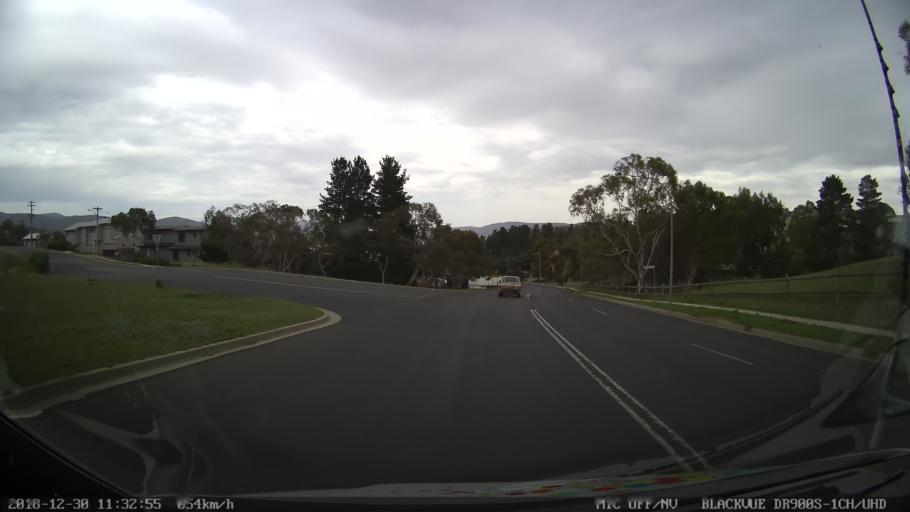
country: AU
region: New South Wales
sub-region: Snowy River
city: Jindabyne
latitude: -36.4181
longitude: 148.6106
